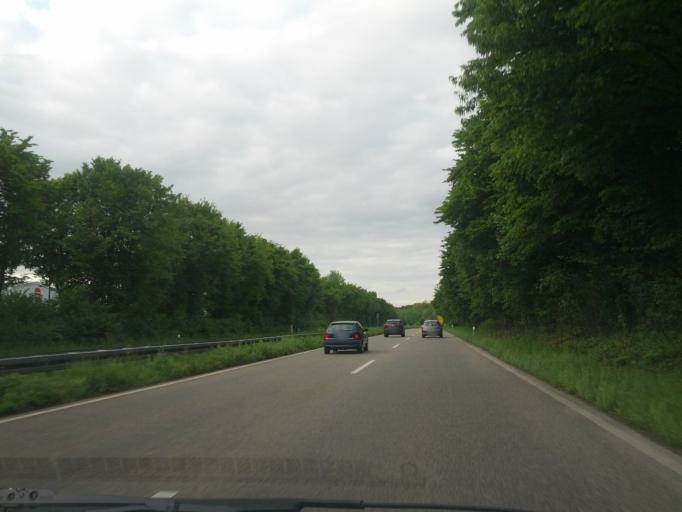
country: DE
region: Baden-Wuerttemberg
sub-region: Freiburg Region
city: Gundelfingen
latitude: 48.0272
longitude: 7.8577
